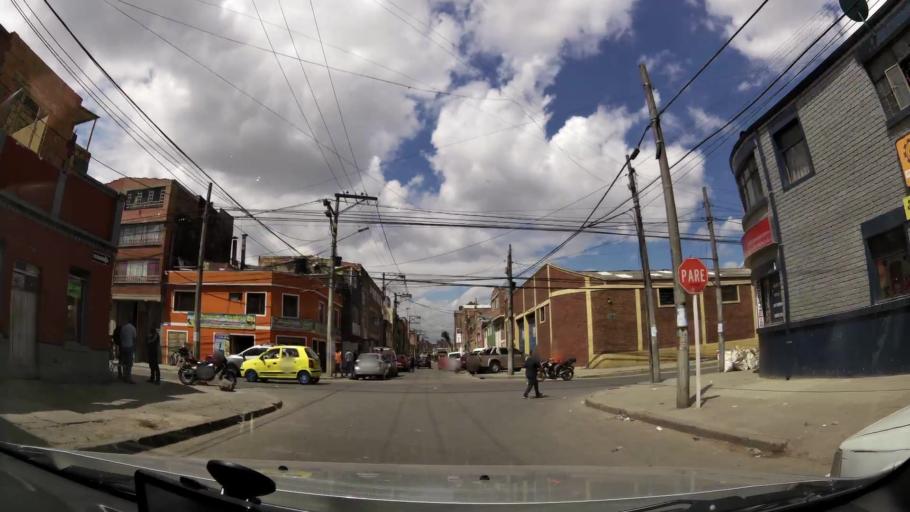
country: CO
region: Bogota D.C.
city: Bogota
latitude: 4.6310
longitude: -74.1070
